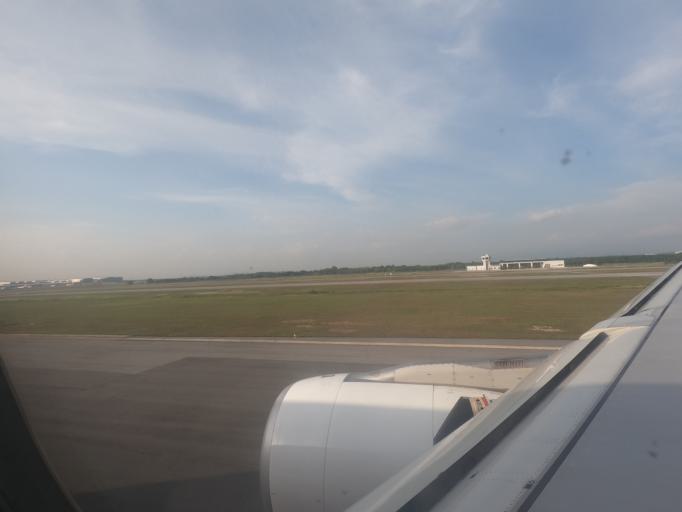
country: MY
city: Sungai Pelek New Village
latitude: 2.7228
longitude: 101.6878
